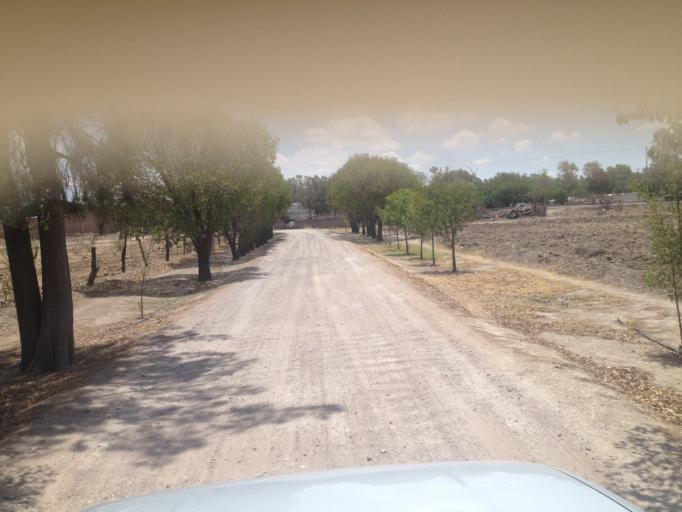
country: MX
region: Aguascalientes
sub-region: Aguascalientes
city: San Sebastian [Fraccionamiento]
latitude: 21.7885
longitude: -102.2831
